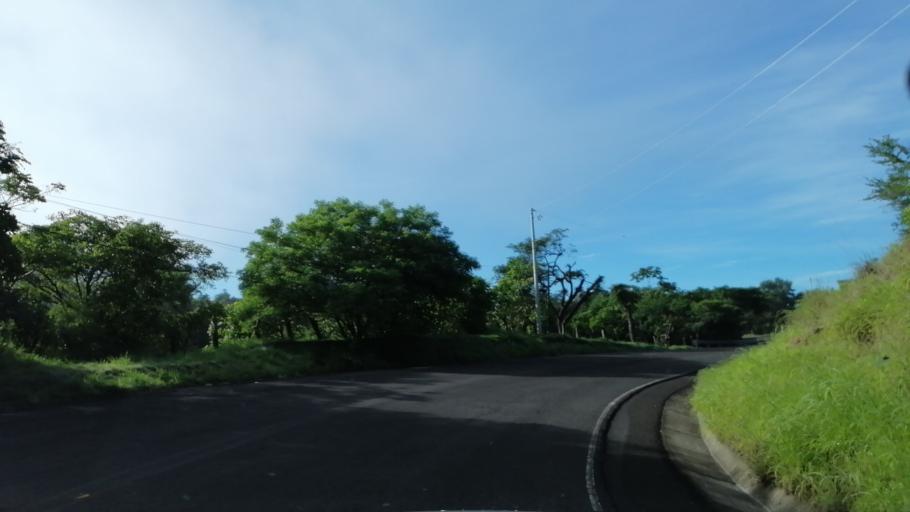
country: SV
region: Morazan
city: Cacaopera
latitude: 13.7863
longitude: -88.1102
